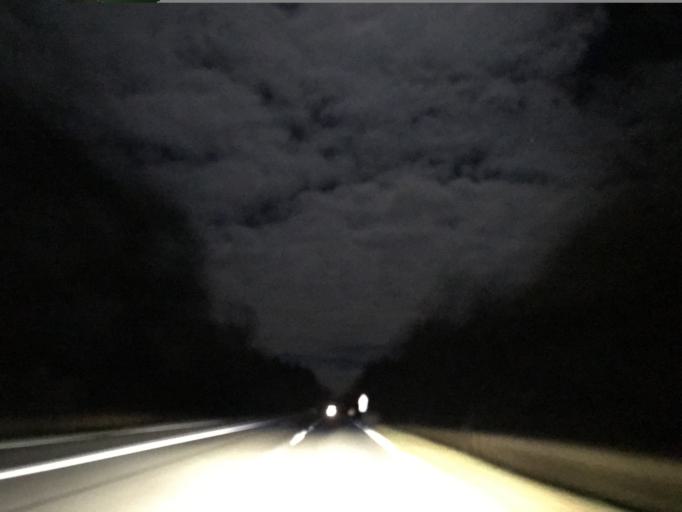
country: FR
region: Auvergne
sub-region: Departement de l'Allier
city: Saint-Yorre
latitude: 46.0143
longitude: 3.4848
